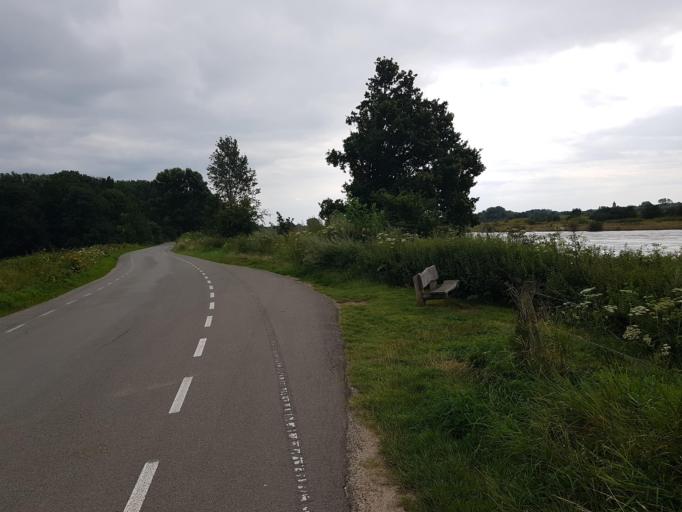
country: NL
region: Gelderland
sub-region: Gemeente Rheden
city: De Steeg
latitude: 52.0111
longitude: 6.0776
